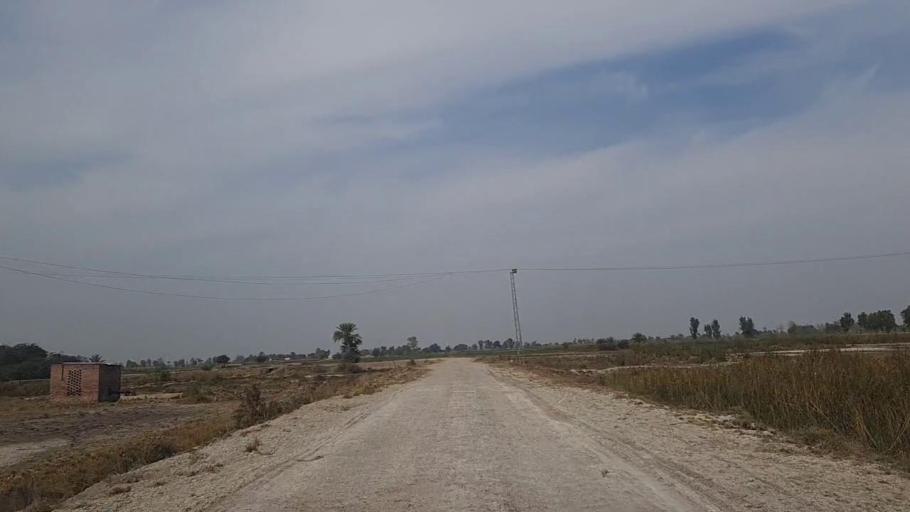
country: PK
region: Sindh
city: Daur
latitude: 26.4818
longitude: 68.4055
